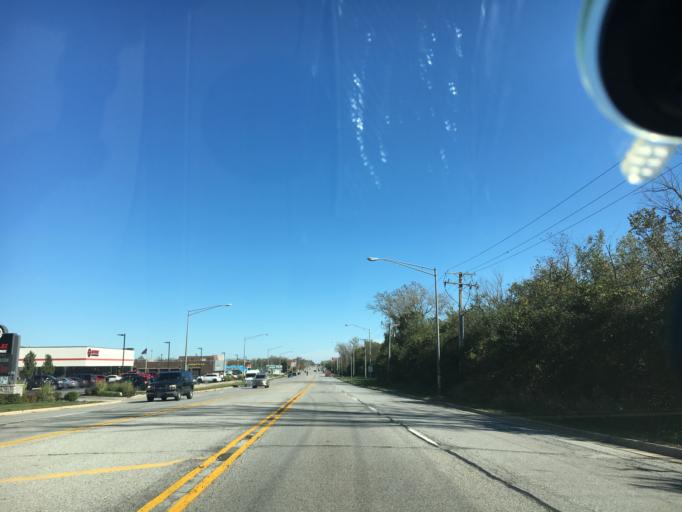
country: US
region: Illinois
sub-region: Cook County
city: Oak Forest
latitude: 41.6028
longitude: -87.7637
